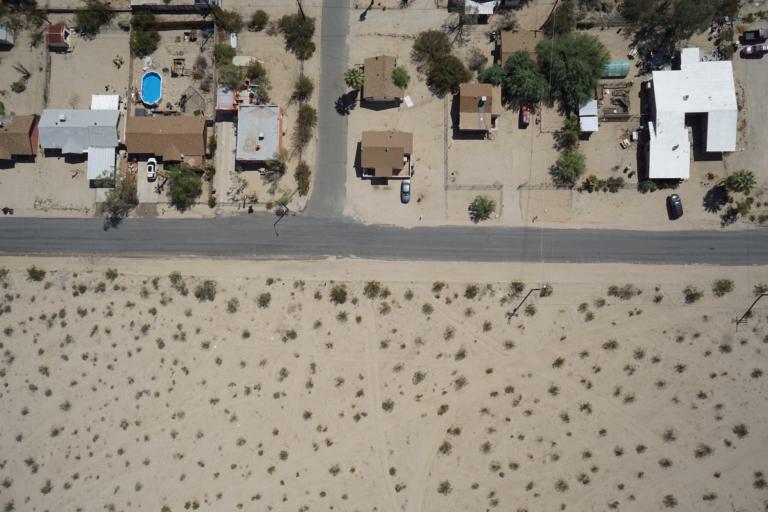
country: US
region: California
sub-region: San Bernardino County
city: Twentynine Palms
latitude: 34.1294
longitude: -116.0324
